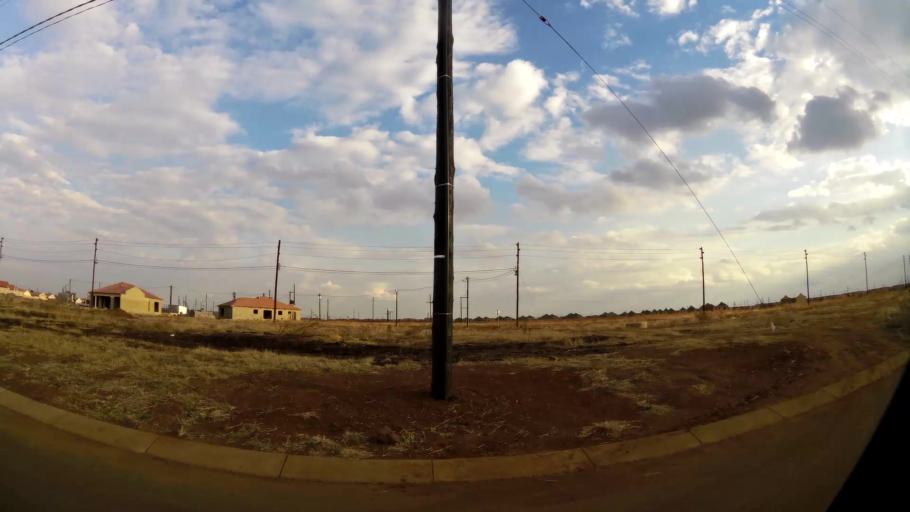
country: ZA
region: Gauteng
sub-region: Sedibeng District Municipality
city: Vanderbijlpark
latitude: -26.6090
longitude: 27.8107
